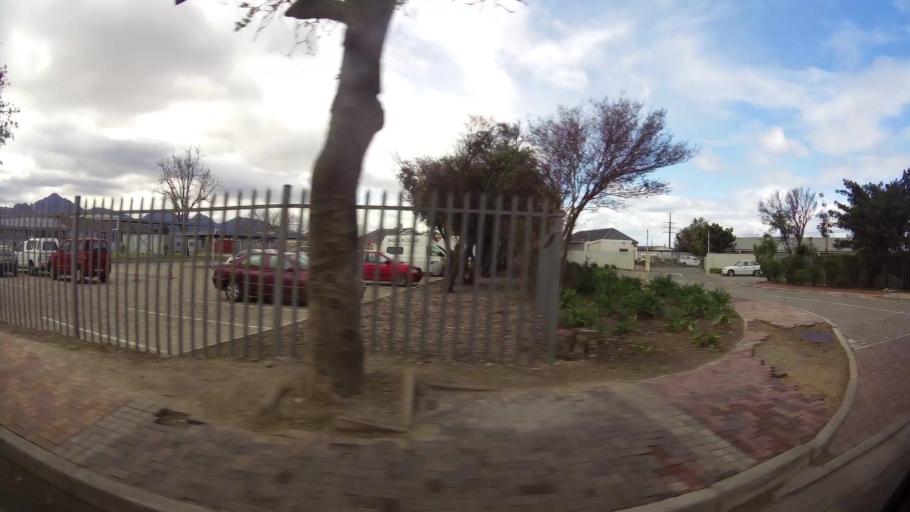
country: ZA
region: Western Cape
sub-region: Eden District Municipality
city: George
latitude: -33.9801
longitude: 22.4718
